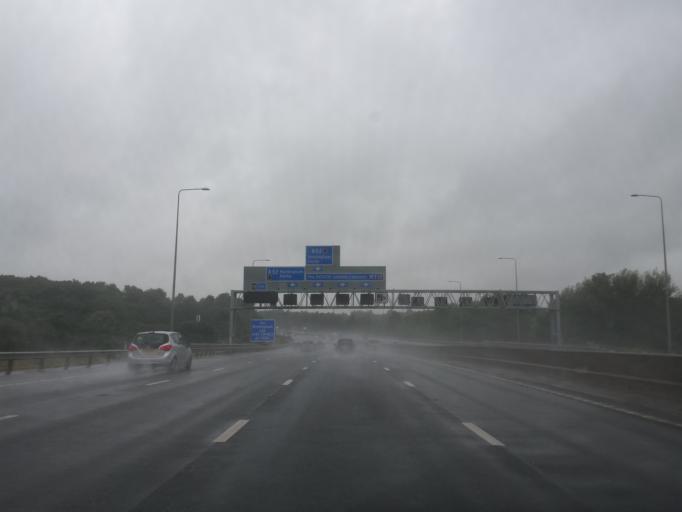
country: GB
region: England
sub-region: Derbyshire
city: Ilkeston
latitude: 52.9374
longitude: -1.2897
